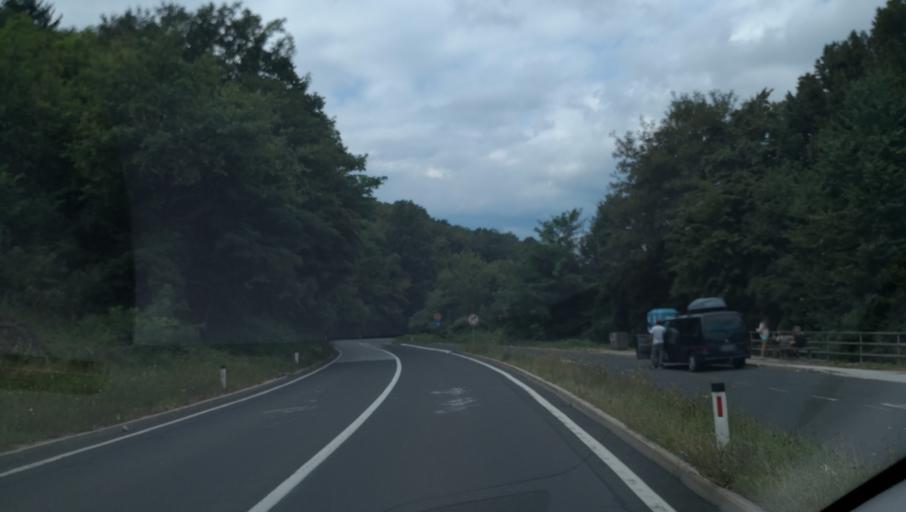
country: SI
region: Novo Mesto
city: Novo Mesto
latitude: 45.7428
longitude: 15.2117
